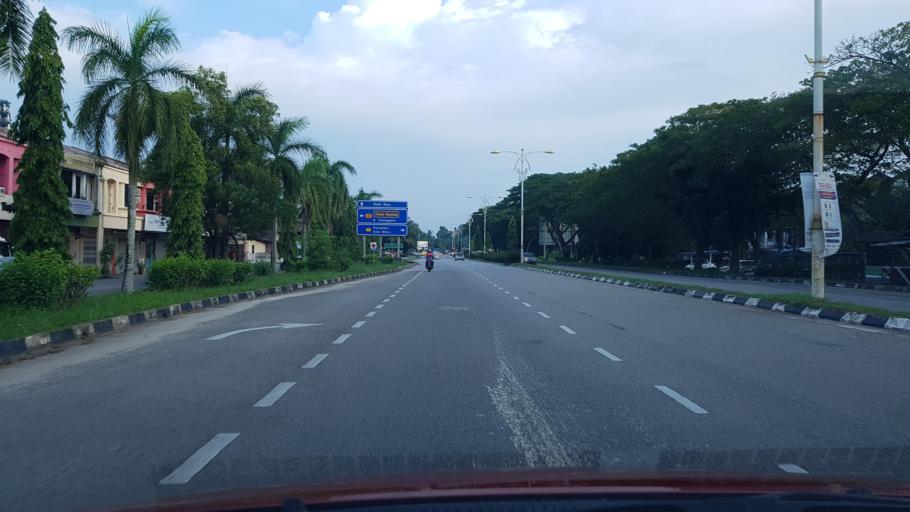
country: MY
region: Terengganu
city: Kuala Terengganu
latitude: 5.3423
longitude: 103.1022
